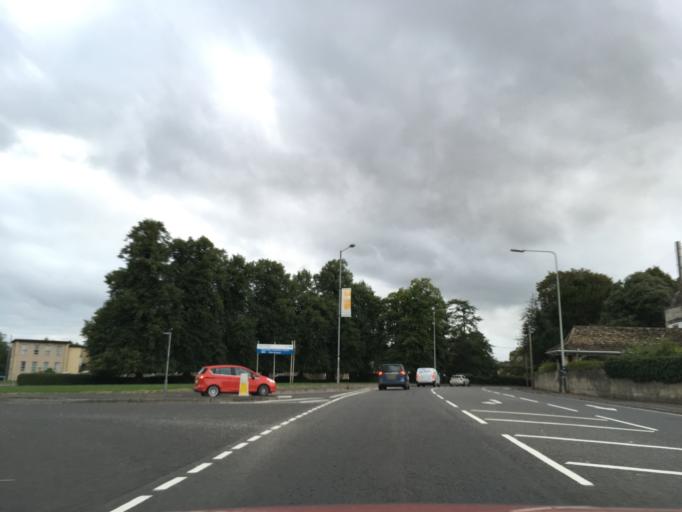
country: GB
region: England
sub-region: Wiltshire
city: Chippenham
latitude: 51.4539
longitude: -2.1256
